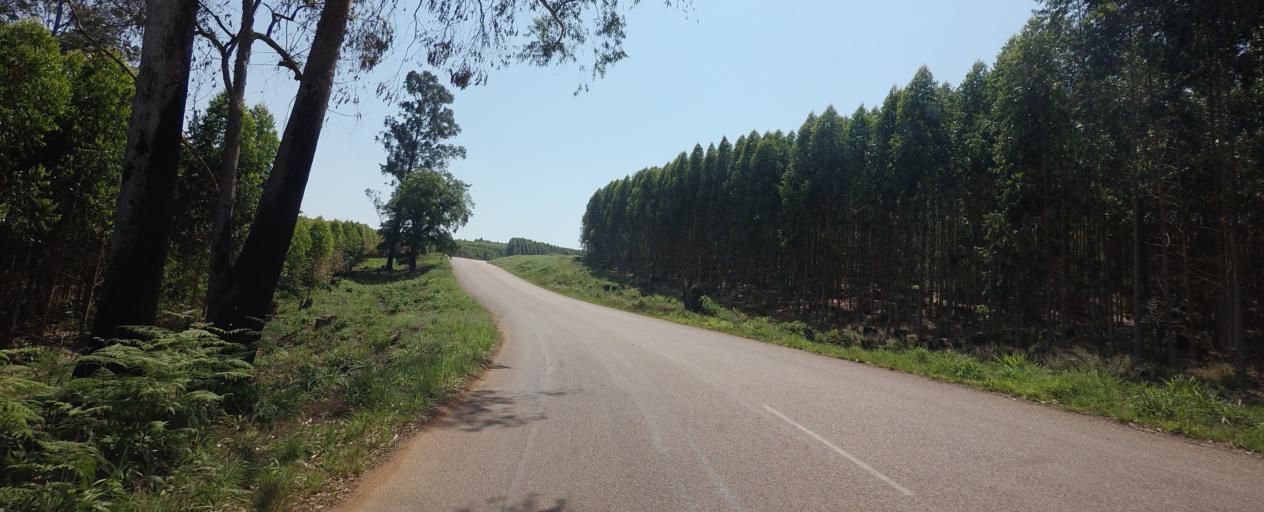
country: ZA
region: Mpumalanga
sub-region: Ehlanzeni District
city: Graksop
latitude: -25.0744
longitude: 30.8017
